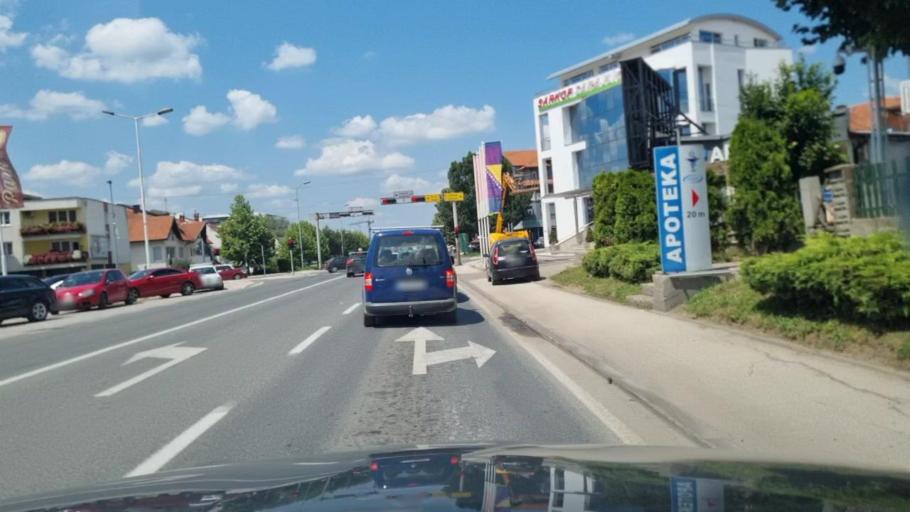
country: BA
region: Federation of Bosnia and Herzegovina
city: Srebrenik
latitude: 44.7042
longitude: 18.4940
